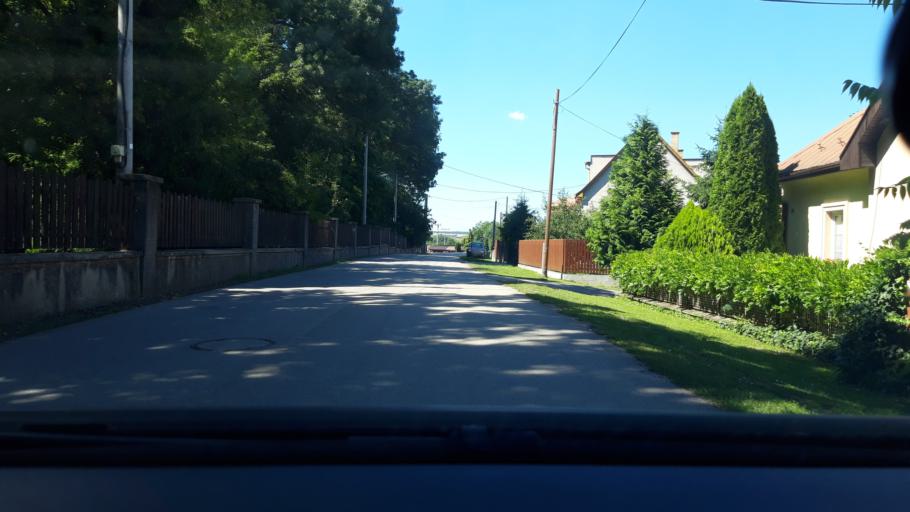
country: SK
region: Nitriansky
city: Partizanske
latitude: 48.6102
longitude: 18.3433
